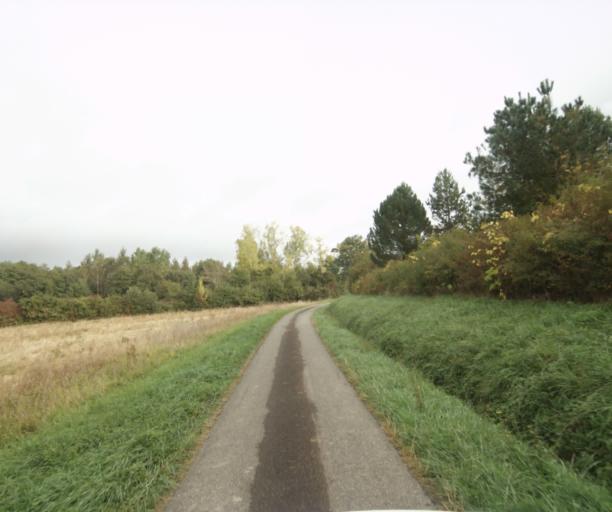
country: FR
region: Midi-Pyrenees
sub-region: Departement du Gers
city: Nogaro
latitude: 43.8260
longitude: -0.0802
